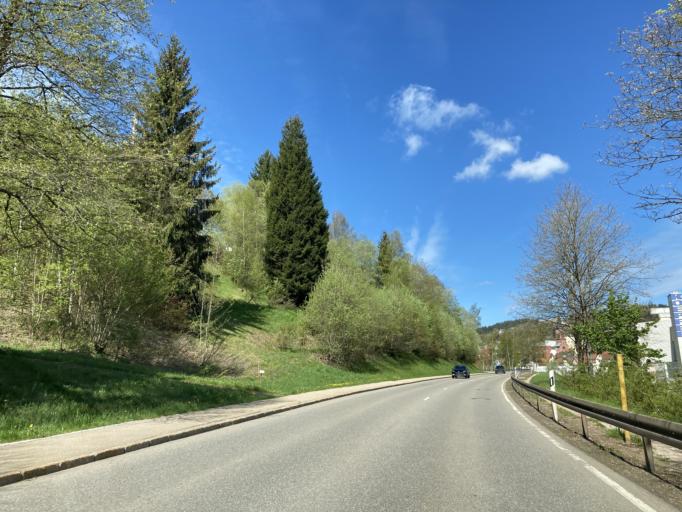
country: DE
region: Baden-Wuerttemberg
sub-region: Freiburg Region
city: Furtwangen im Schwarzwald
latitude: 48.0481
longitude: 8.2123
